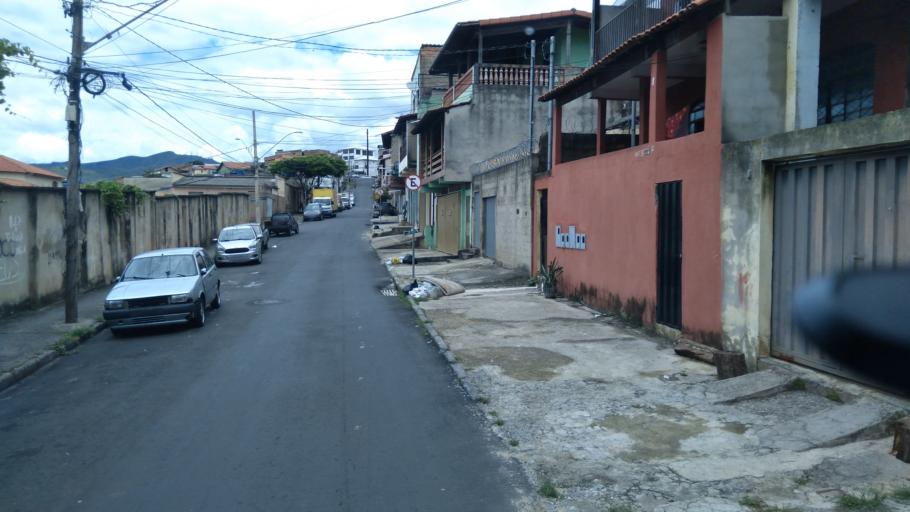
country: BR
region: Minas Gerais
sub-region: Belo Horizonte
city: Belo Horizonte
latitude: -19.8949
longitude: -43.8889
